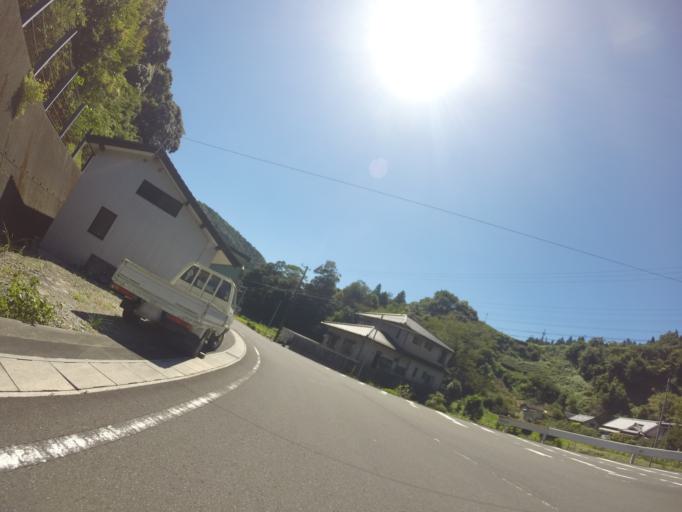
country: JP
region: Shizuoka
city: Kanaya
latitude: 34.8914
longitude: 138.1484
